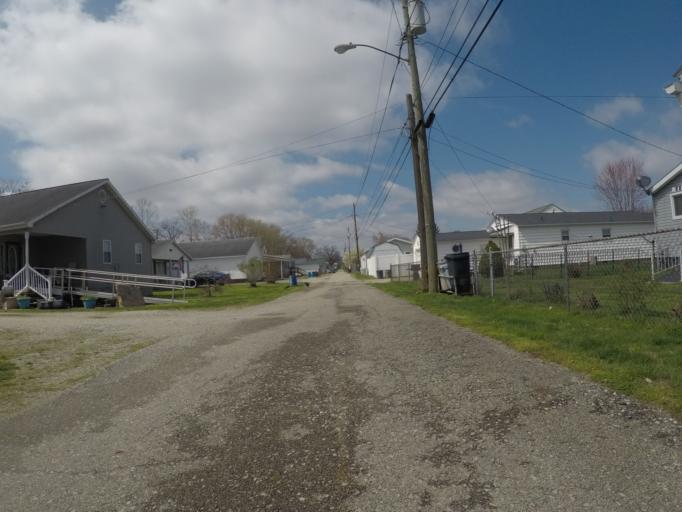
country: US
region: West Virginia
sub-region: Wayne County
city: Ceredo
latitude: 38.3958
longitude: -82.5679
